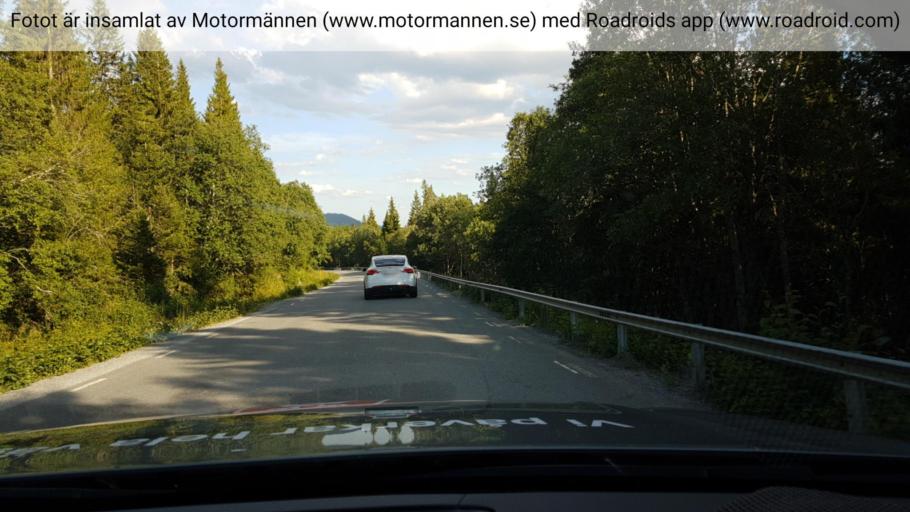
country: SE
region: Jaemtland
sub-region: Are Kommun
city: Are
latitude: 63.4115
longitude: 13.0382
